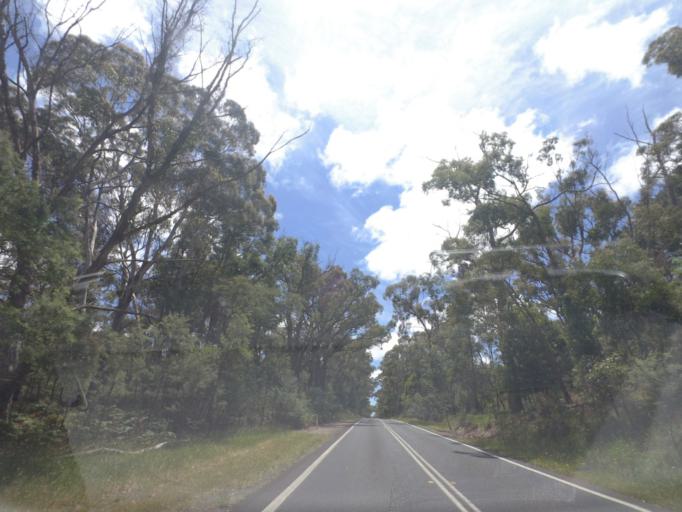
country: AU
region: Victoria
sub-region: Mount Alexander
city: Castlemaine
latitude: -37.3107
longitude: 144.1657
